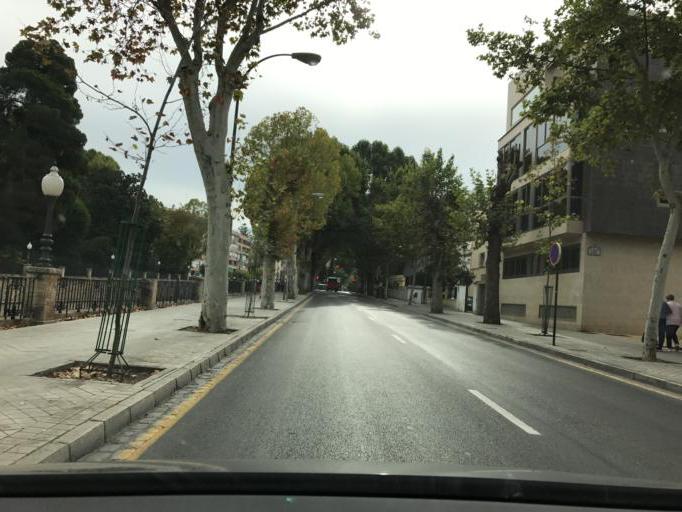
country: ES
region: Andalusia
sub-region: Provincia de Granada
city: Granada
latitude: 37.1681
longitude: -3.5911
